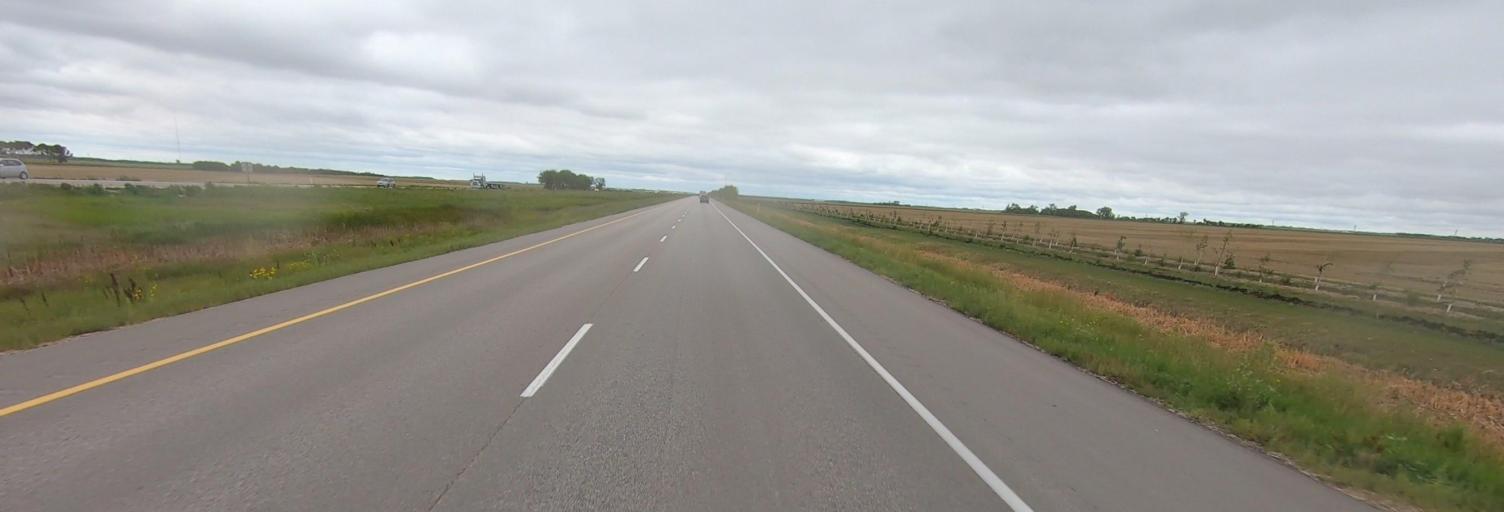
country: CA
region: Manitoba
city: Headingley
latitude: 49.8883
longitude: -97.6572
